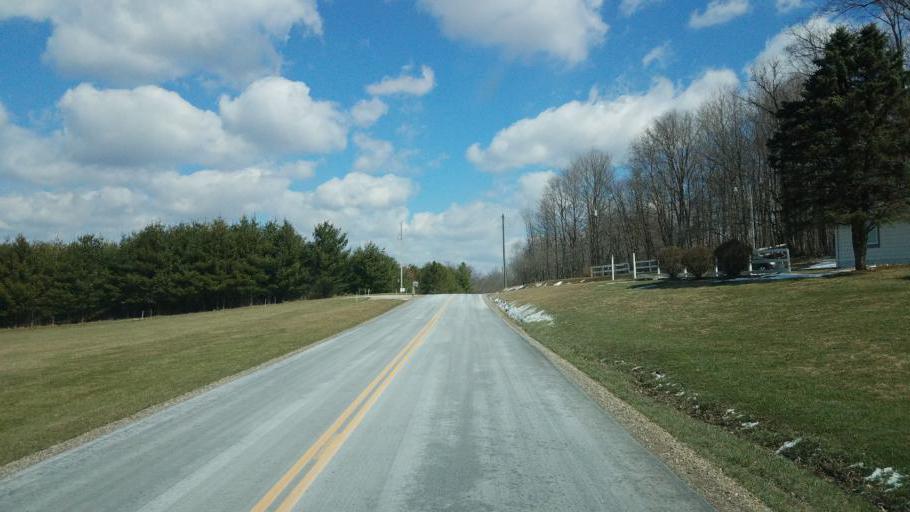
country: US
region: Ohio
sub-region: Knox County
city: Mount Vernon
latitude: 40.3386
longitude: -82.5599
